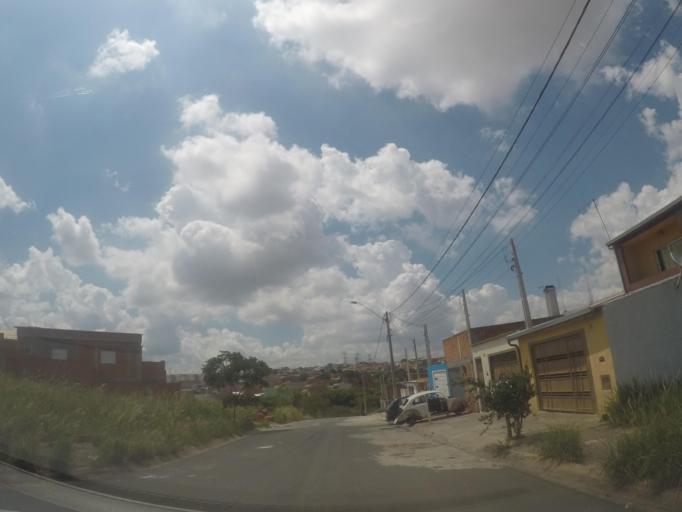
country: BR
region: Sao Paulo
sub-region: Hortolandia
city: Hortolandia
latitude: -22.8411
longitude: -47.2030
